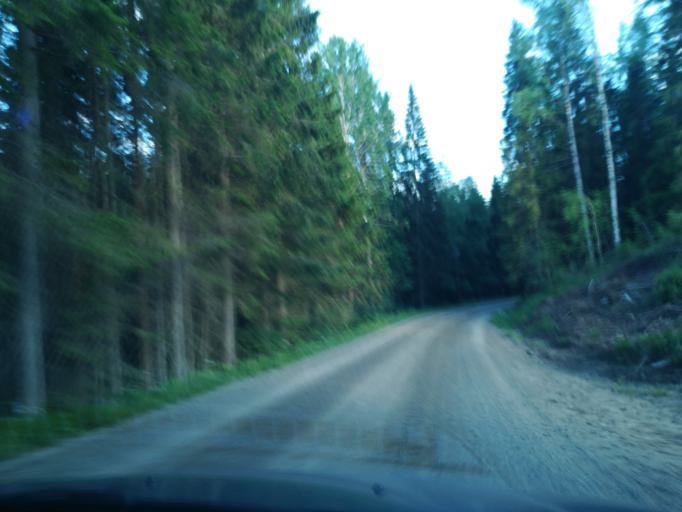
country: FI
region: Southern Savonia
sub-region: Mikkeli
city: Puumala
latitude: 61.6272
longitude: 28.1082
